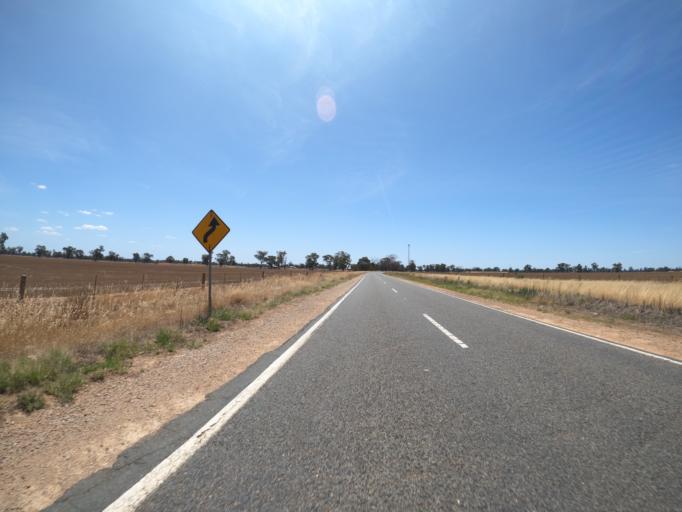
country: AU
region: Victoria
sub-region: Moira
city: Yarrawonga
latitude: -36.1928
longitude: 145.9670
